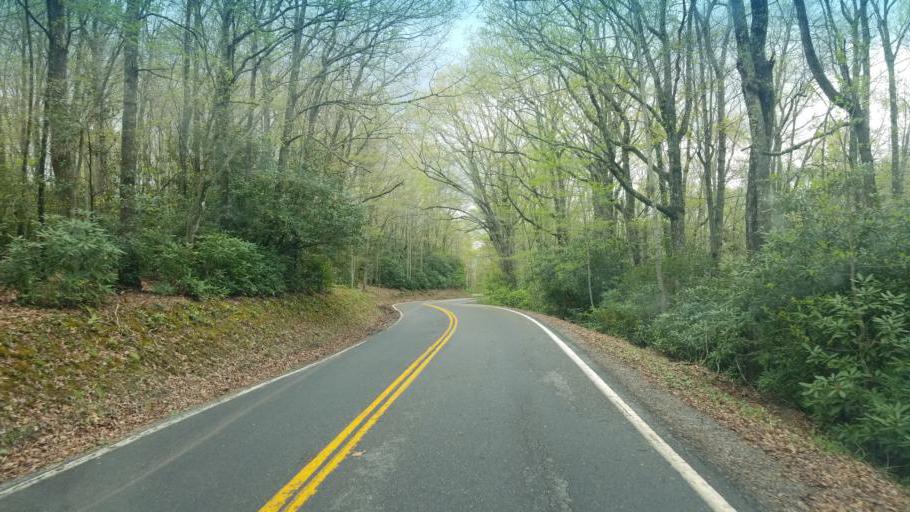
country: US
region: Virginia
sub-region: Tazewell County
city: Tazewell
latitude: 36.9864
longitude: -81.5296
